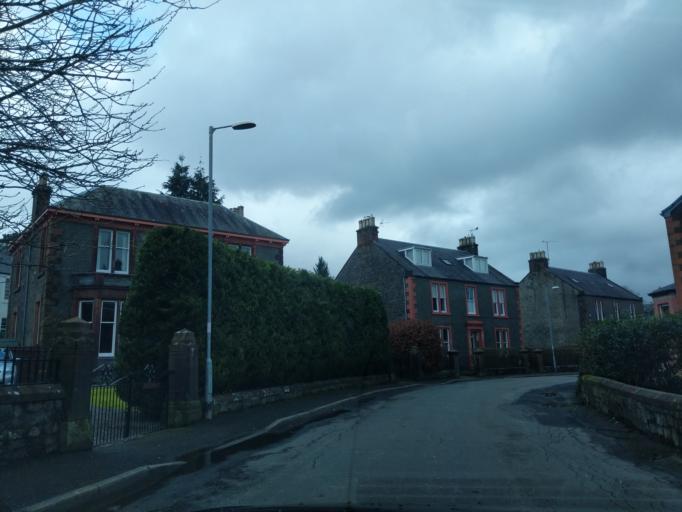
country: GB
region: Scotland
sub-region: Dumfries and Galloway
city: Moffat
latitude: 55.3329
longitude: -3.4423
